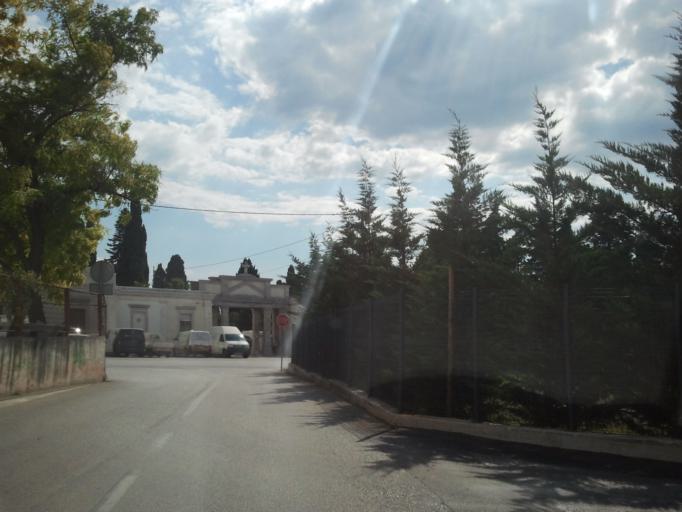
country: HR
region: Zadarska
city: Zadar
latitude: 44.1056
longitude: 15.2581
